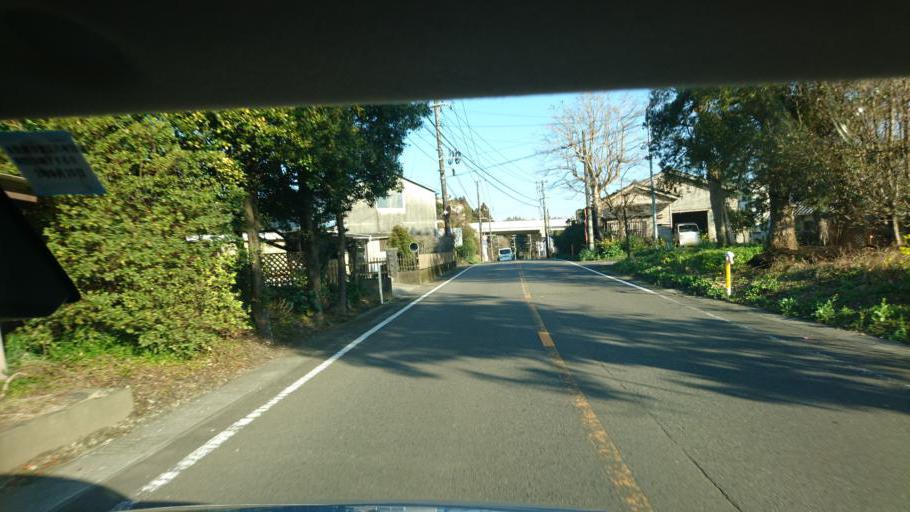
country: JP
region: Miyazaki
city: Miyazaki-shi
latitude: 31.8543
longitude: 131.3740
